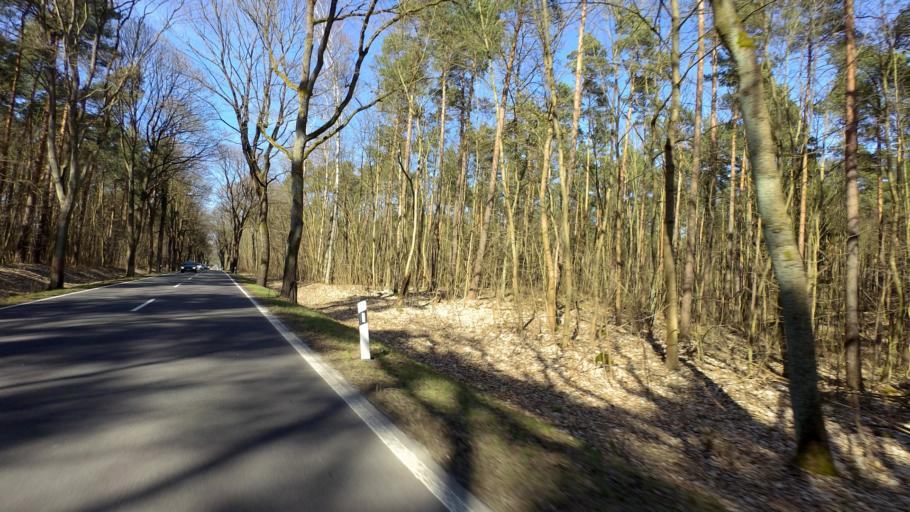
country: DE
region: Brandenburg
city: Waldsieversdorf
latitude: 52.5512
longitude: 14.0429
